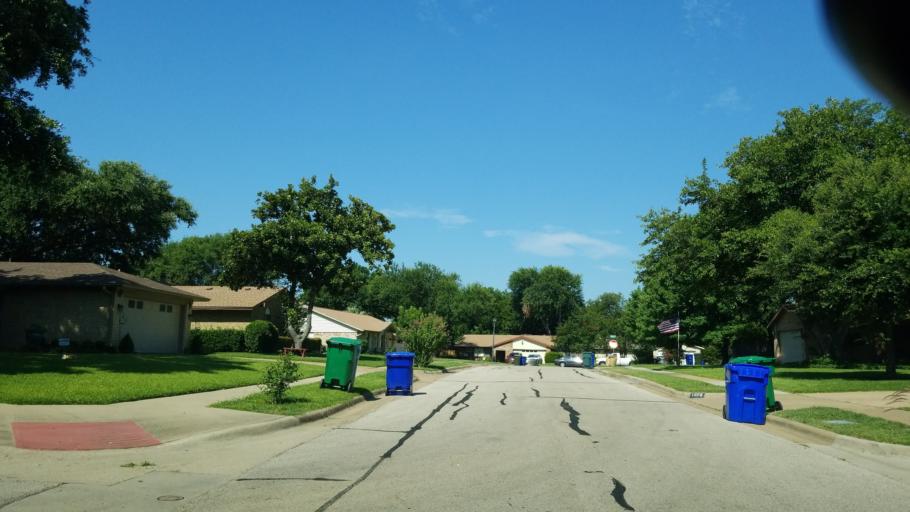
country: US
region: Texas
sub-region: Dallas County
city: Carrollton
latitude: 32.9623
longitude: -96.9059
